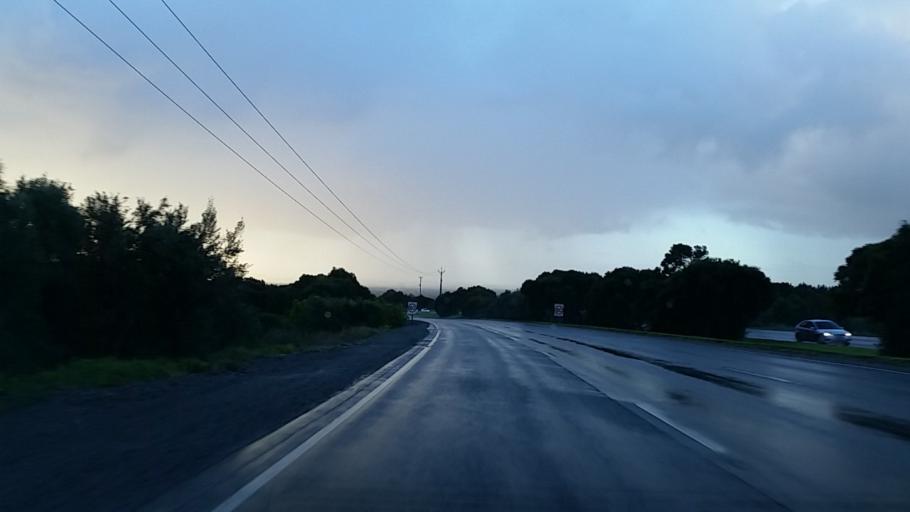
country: AU
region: South Australia
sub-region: Onkaparinga
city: Bedford Park
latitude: -35.0449
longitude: 138.5608
